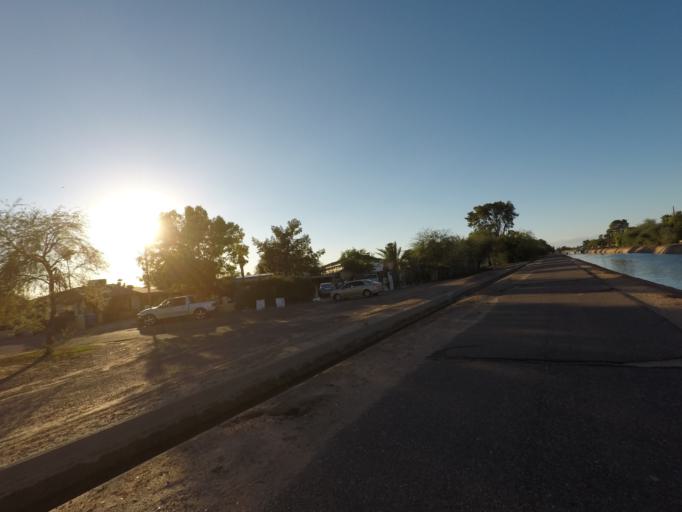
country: US
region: Arizona
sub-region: Maricopa County
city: Phoenix
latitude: 33.4710
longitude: -112.0229
